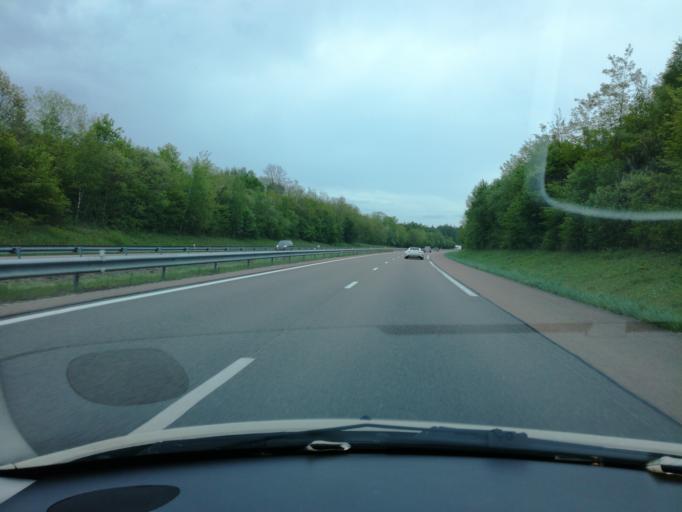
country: FR
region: Franche-Comte
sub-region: Departement du Jura
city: Mont-sous-Vaudrey
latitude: 46.9433
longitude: 5.5525
